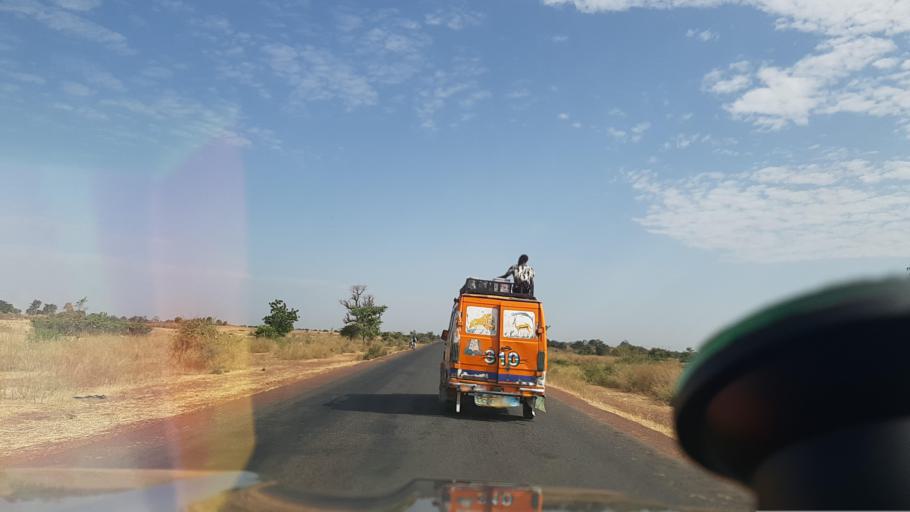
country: ML
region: Segou
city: Markala
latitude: 13.6942
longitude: -6.0987
